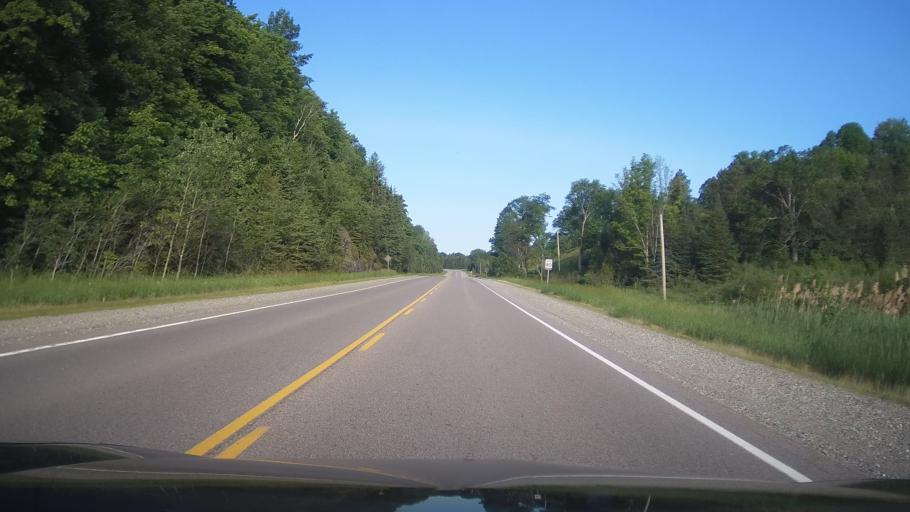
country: CA
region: Ontario
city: Skatepark
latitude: 44.7569
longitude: -76.8055
